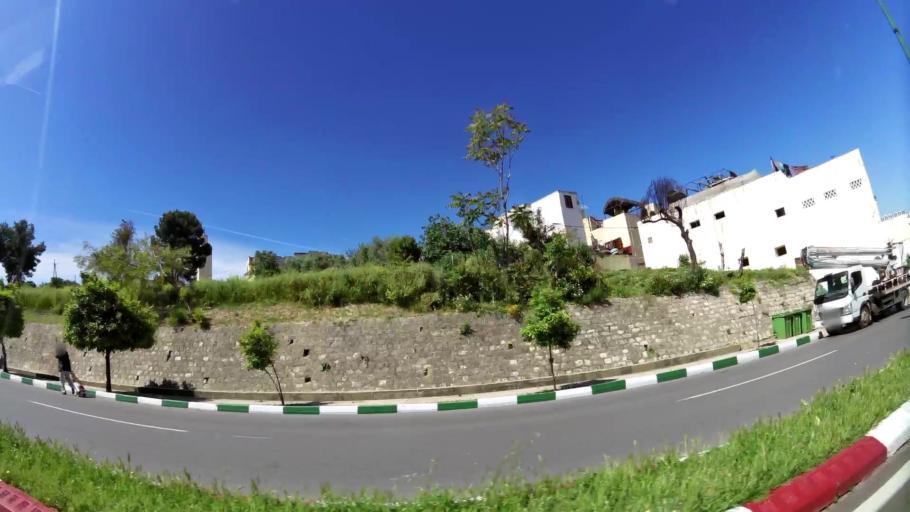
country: MA
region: Meknes-Tafilalet
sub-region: Meknes
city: Meknes
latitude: 33.8920
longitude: -5.5538
